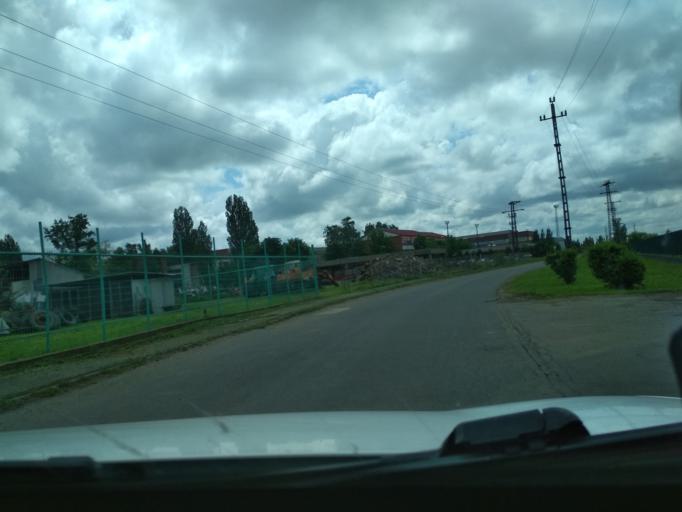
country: HU
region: Jasz-Nagykun-Szolnok
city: Tiszafured
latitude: 47.6106
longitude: 20.7317
